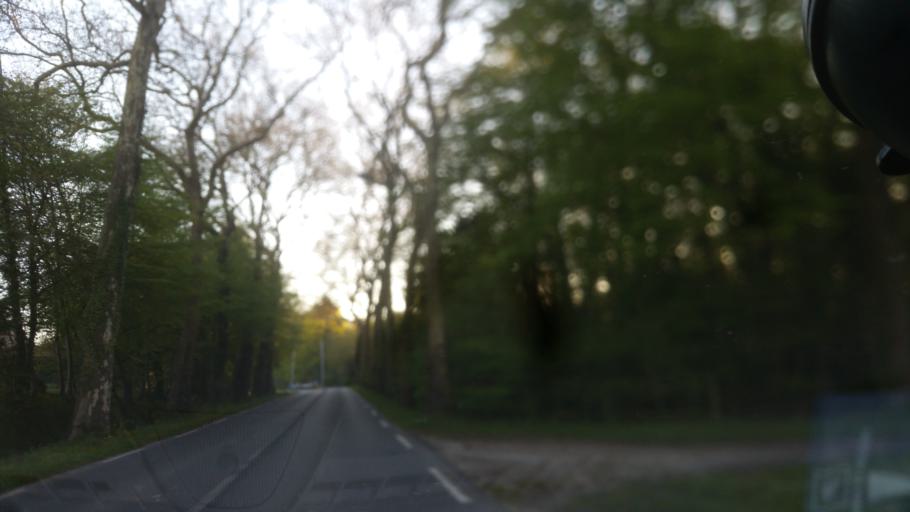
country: FR
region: Ile-de-France
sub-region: Departement de l'Essonne
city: Angervilliers
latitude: 48.5900
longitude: 2.0613
